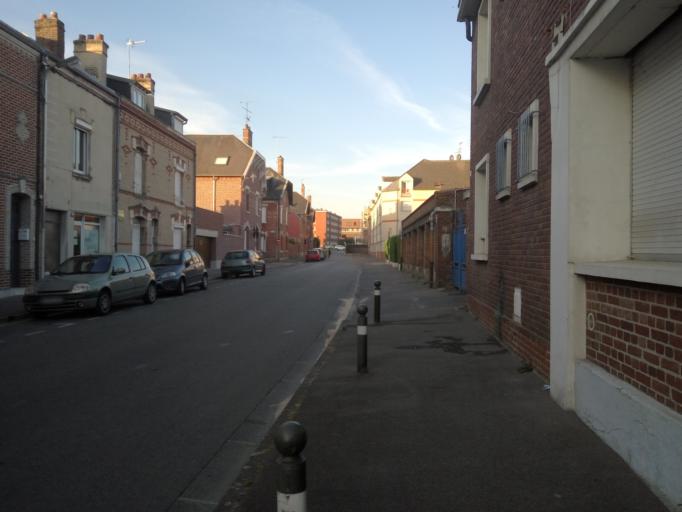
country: FR
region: Picardie
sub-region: Departement de la Somme
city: Amiens
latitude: 49.8954
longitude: 2.2853
